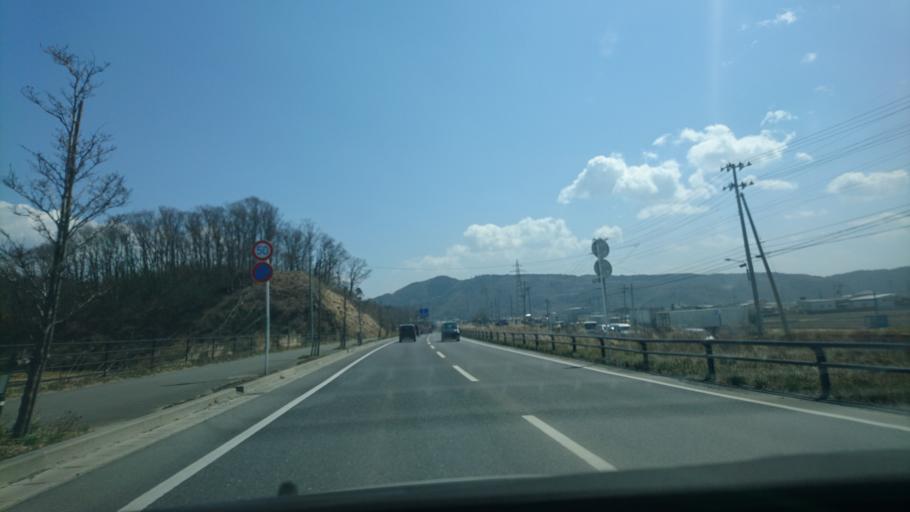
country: JP
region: Miyagi
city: Ishinomaki
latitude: 38.4540
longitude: 141.3094
